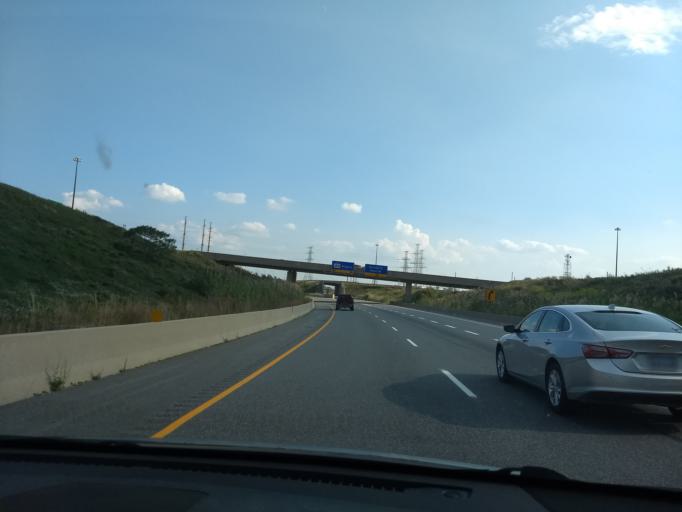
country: CA
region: Ontario
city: Burlington
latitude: 43.3366
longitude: -79.8318
